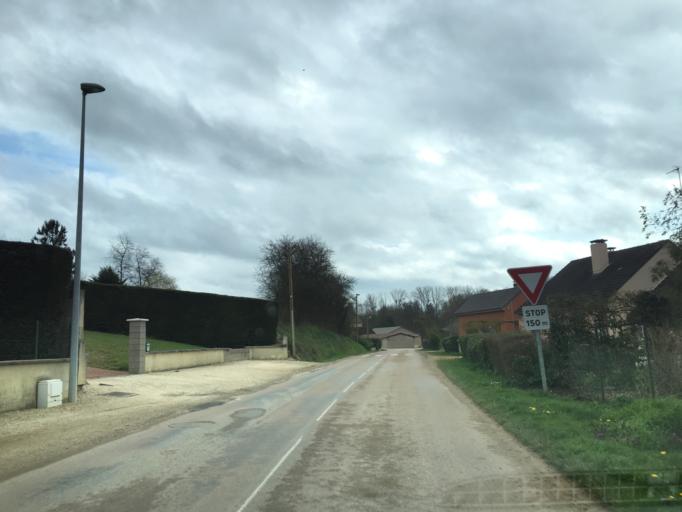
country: FR
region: Bourgogne
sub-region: Departement de l'Yonne
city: Pourrain
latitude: 47.7970
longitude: 3.3827
